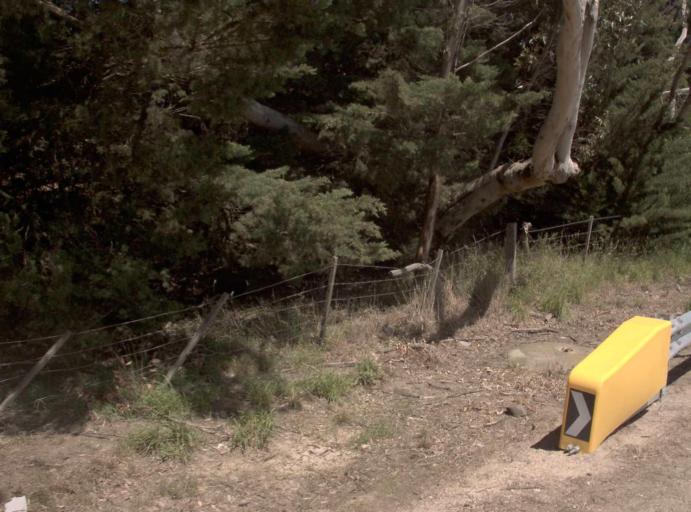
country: AU
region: Victoria
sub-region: Wellington
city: Heyfield
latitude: -38.0429
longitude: 146.8767
